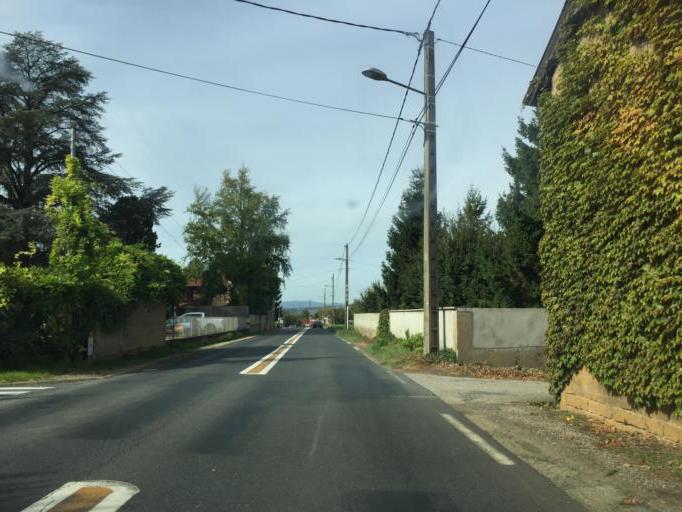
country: FR
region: Rhone-Alpes
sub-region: Departement du Rhone
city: Chasselay
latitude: 45.8725
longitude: 4.7626
